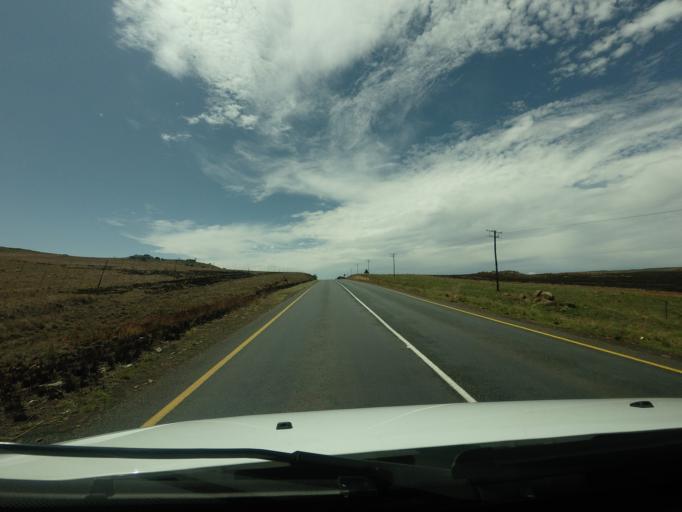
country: ZA
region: Mpumalanga
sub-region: Nkangala District Municipality
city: Belfast
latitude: -25.4031
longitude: 30.1213
